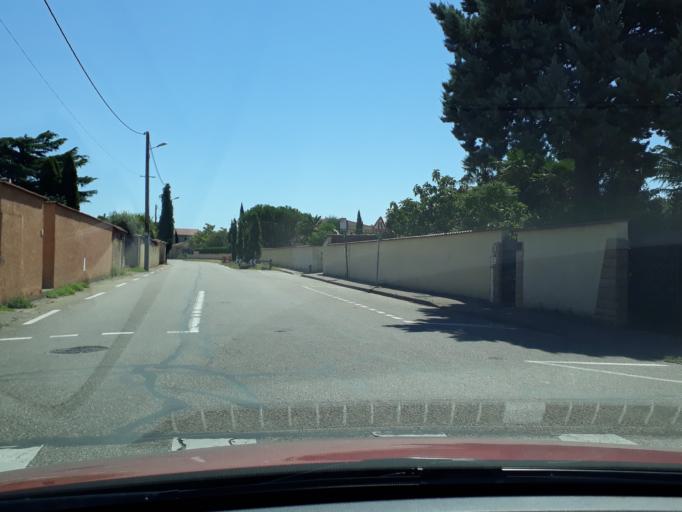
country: FR
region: Rhone-Alpes
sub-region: Departement du Rhone
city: Genas
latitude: 45.7007
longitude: 4.9814
